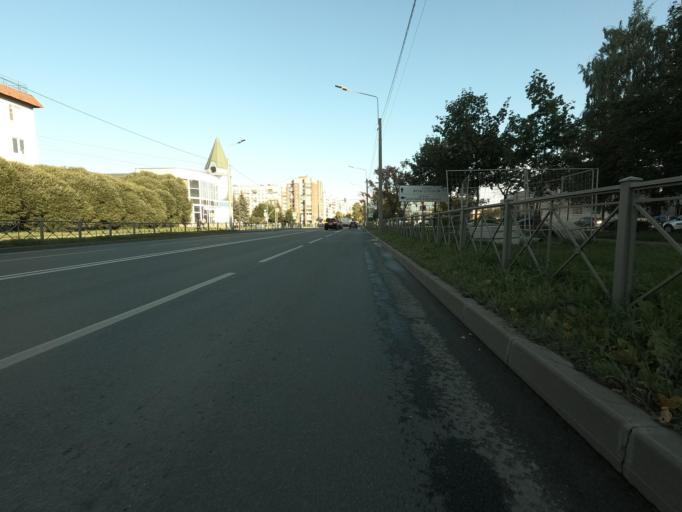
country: RU
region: St.-Petersburg
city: Kolpino
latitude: 59.7416
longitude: 30.5772
